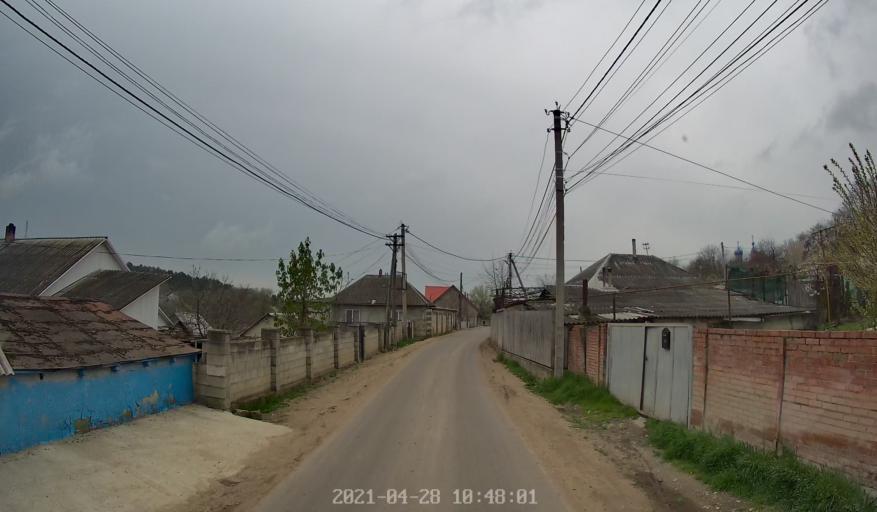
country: MD
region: Chisinau
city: Singera
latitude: 46.9863
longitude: 28.9458
